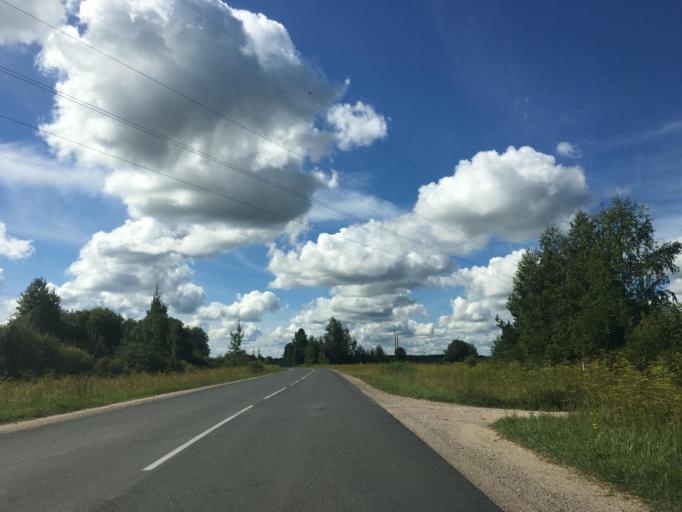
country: RU
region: Pskov
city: Pskov
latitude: 57.7753
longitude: 28.1640
